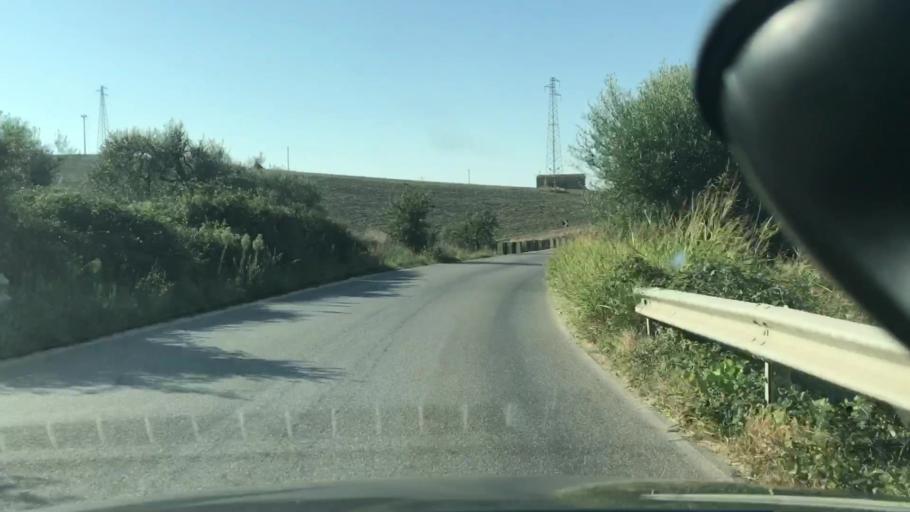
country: IT
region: Basilicate
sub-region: Provincia di Matera
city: Matera
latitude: 40.6609
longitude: 16.5706
